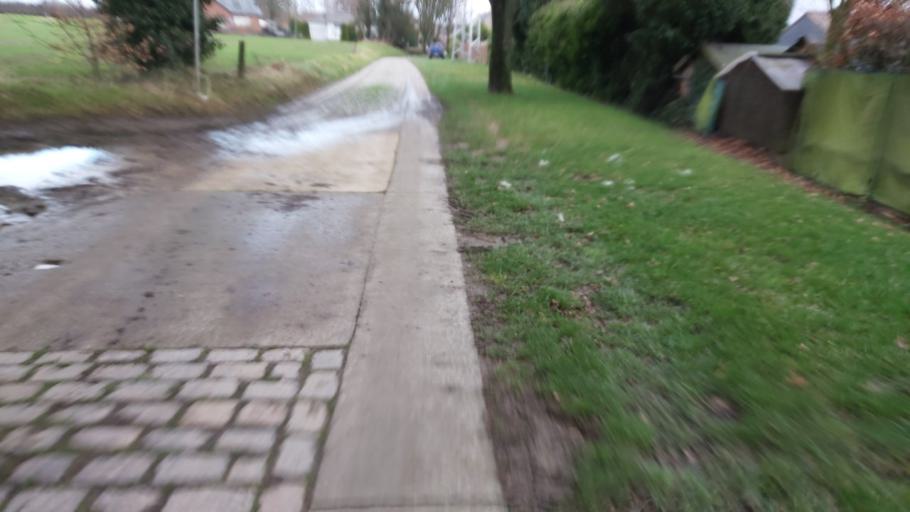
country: BE
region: Flanders
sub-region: Provincie Vlaams-Brabant
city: Tienen
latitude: 50.8238
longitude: 4.9317
